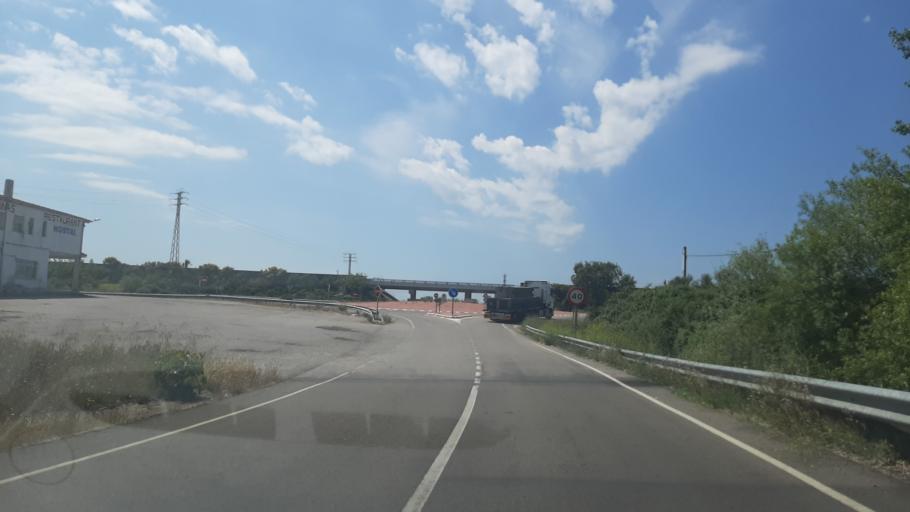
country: ES
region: Castille and Leon
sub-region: Provincia de Salamanca
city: Espeja
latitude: 40.5922
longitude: -6.7053
